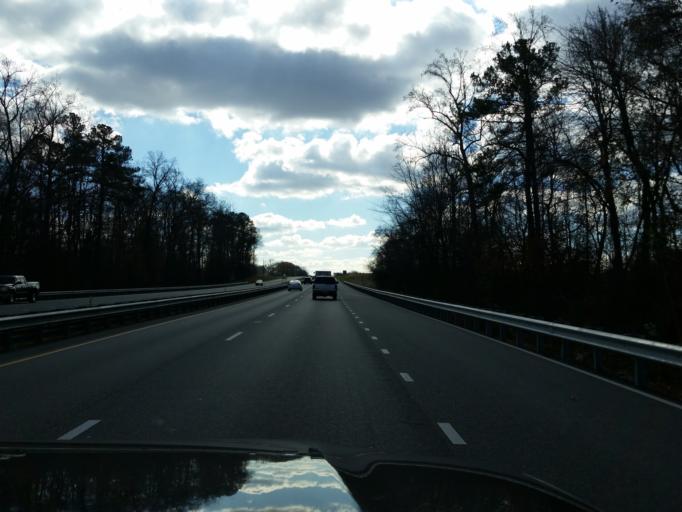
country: US
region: Maryland
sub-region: Talbot County
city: Easton
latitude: 38.8507
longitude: -76.0609
